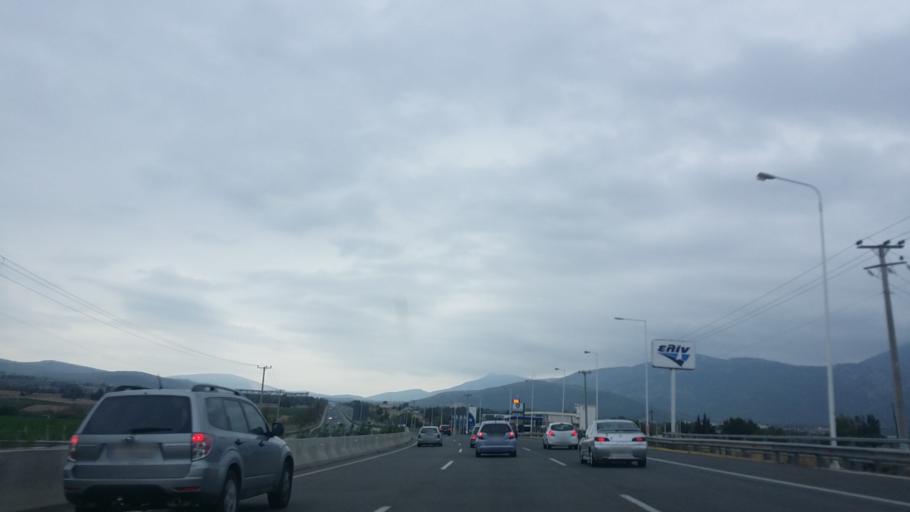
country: GR
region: Attica
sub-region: Nomarchia Anatolikis Attikis
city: Avlonas
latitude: 38.2707
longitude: 23.6964
